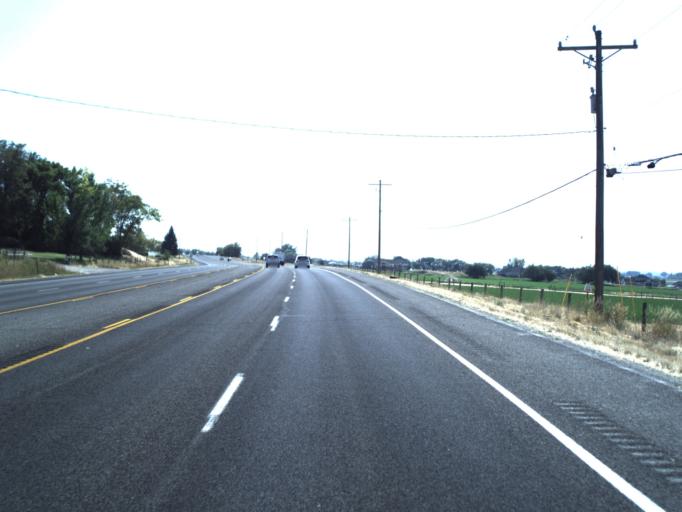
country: US
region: Utah
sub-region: Cache County
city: Smithfield
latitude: 41.8716
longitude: -111.8270
